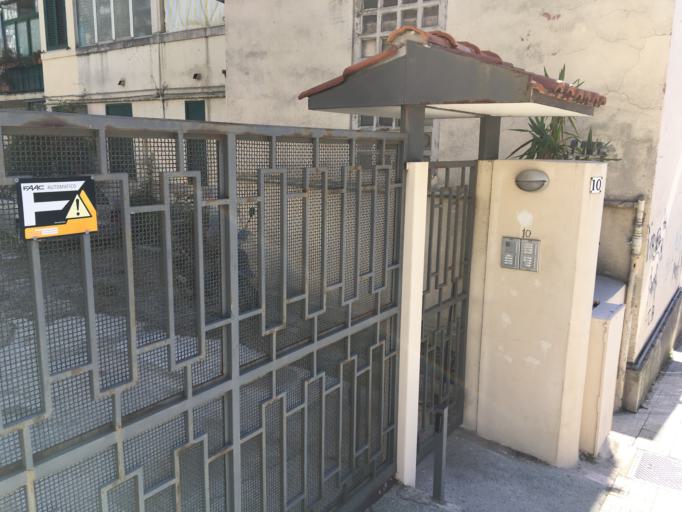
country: IT
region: Sicily
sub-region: Messina
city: Messina
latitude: 38.1958
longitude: 15.5502
